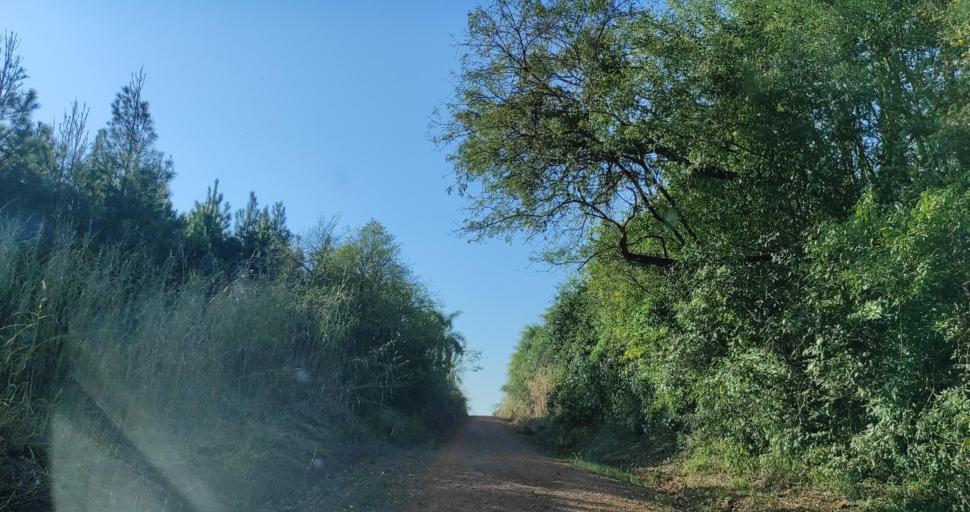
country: AR
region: Misiones
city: Capiovi
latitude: -26.8829
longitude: -55.1076
